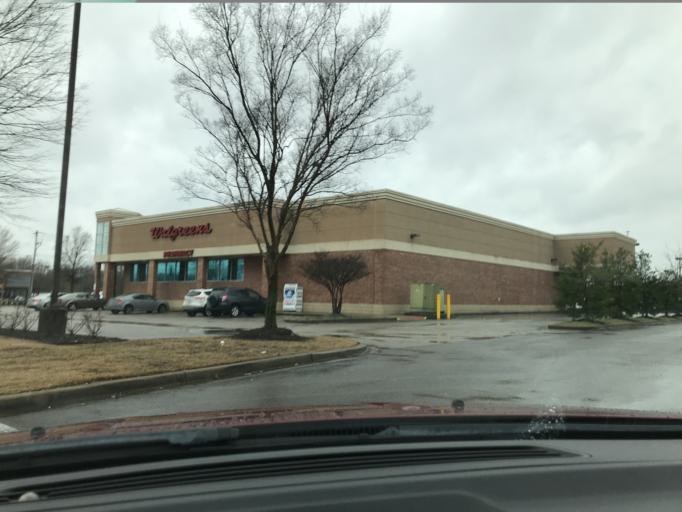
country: US
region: Tennessee
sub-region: Shelby County
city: Collierville
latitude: 35.0482
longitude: -89.7328
